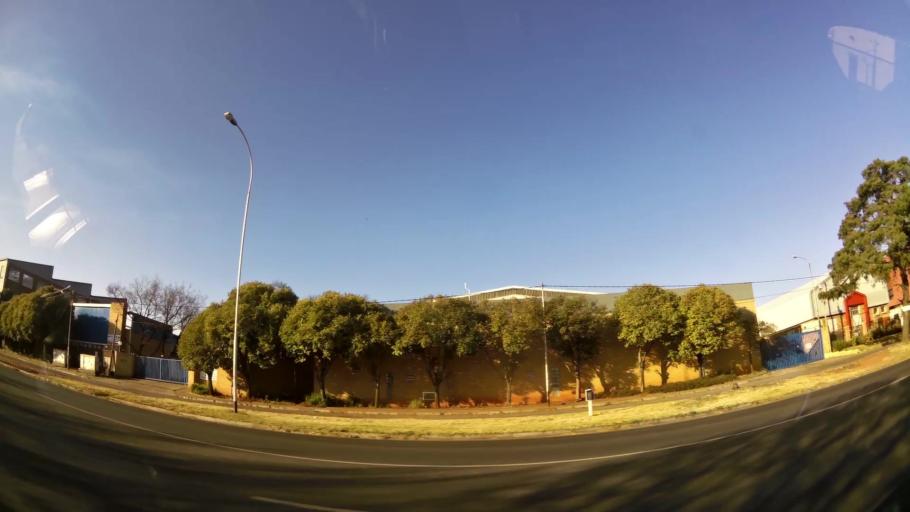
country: ZA
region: Gauteng
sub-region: City of Johannesburg Metropolitan Municipality
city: Roodepoort
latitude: -26.1465
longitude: 27.8624
